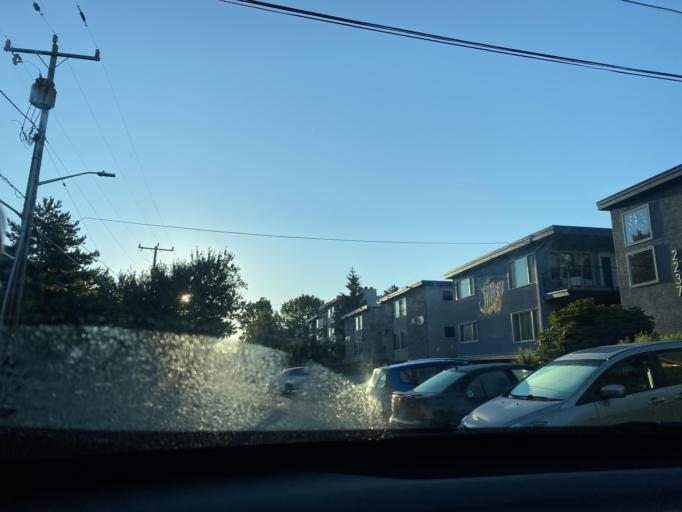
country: US
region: Washington
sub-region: King County
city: Seattle
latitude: 47.6716
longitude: -122.3862
